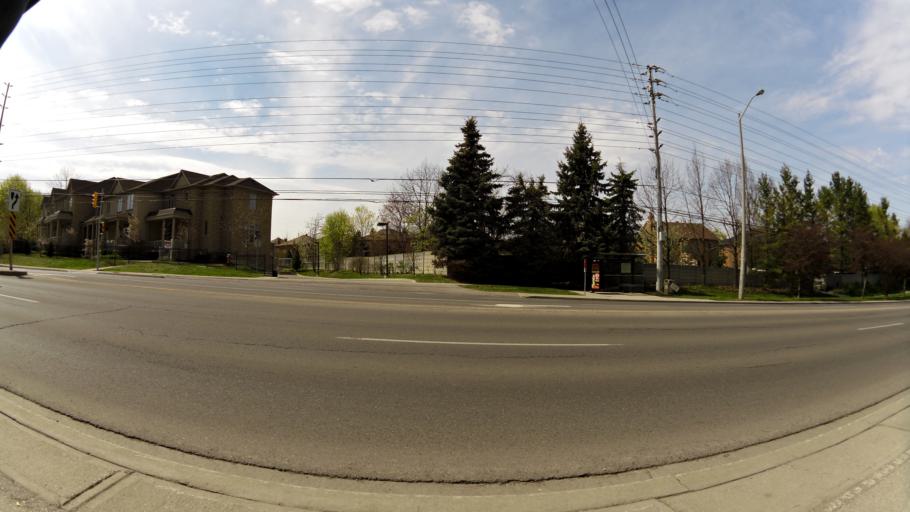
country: CA
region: Ontario
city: Mississauga
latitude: 43.5321
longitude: -79.6068
